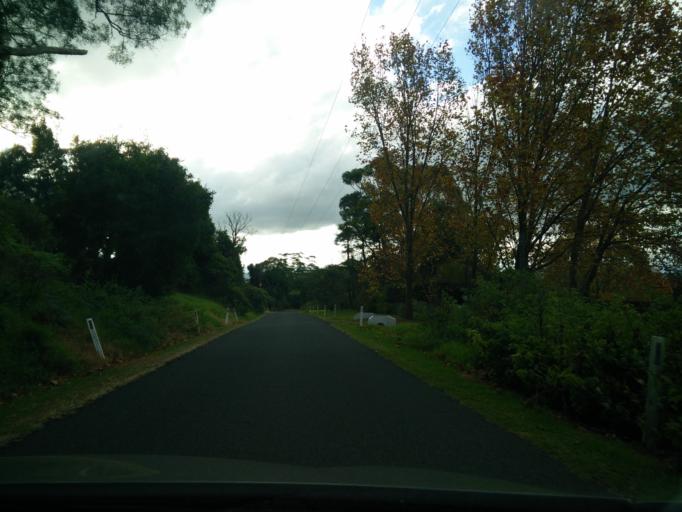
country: AU
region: New South Wales
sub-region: Kiama
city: Jamberoo
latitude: -34.6910
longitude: 150.7876
